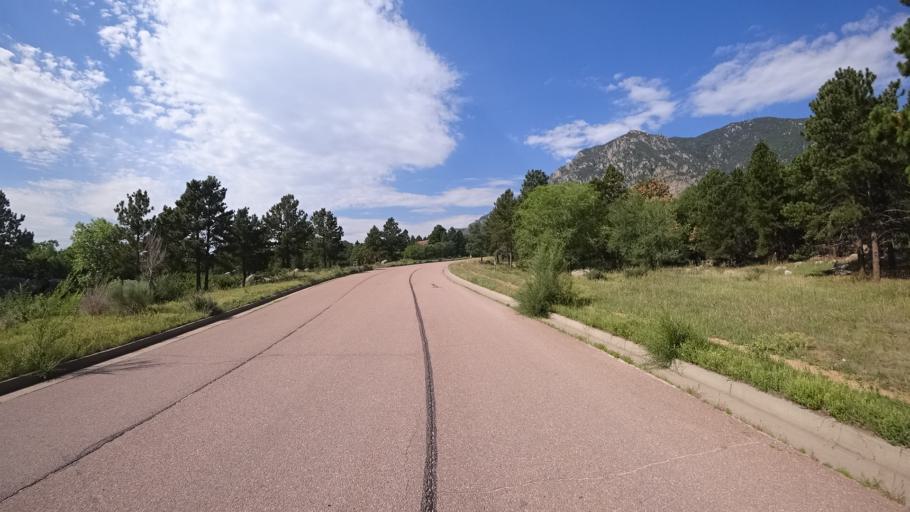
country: US
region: Colorado
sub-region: El Paso County
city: Fort Carson
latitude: 38.7464
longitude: -104.8301
